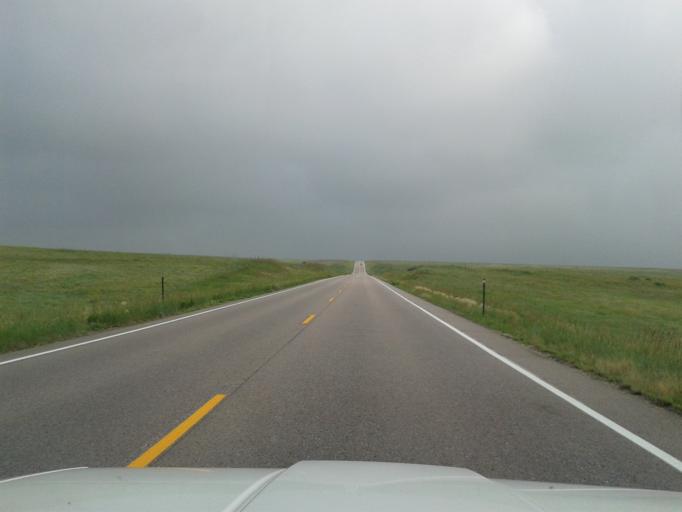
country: US
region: Colorado
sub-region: Elbert County
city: Ponderosa Park
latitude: 39.2959
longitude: -104.7360
